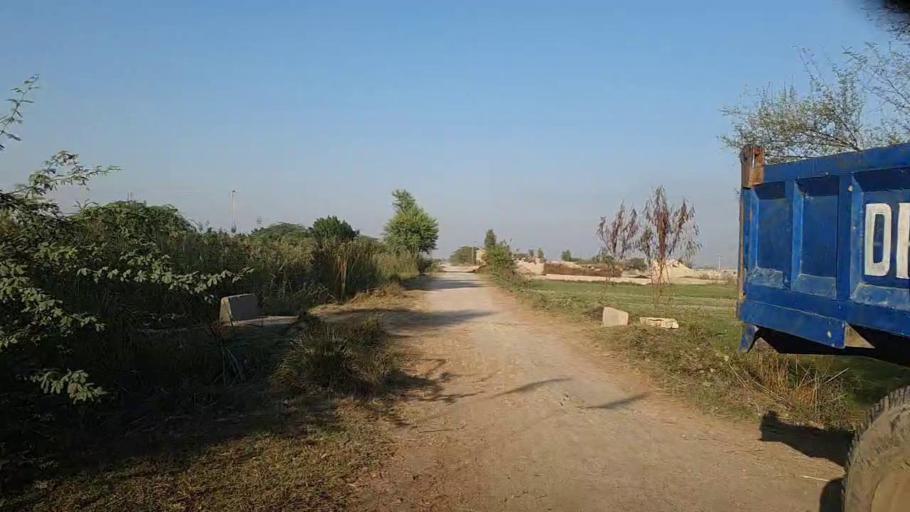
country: PK
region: Sindh
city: Ranipur
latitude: 27.2503
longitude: 68.5068
